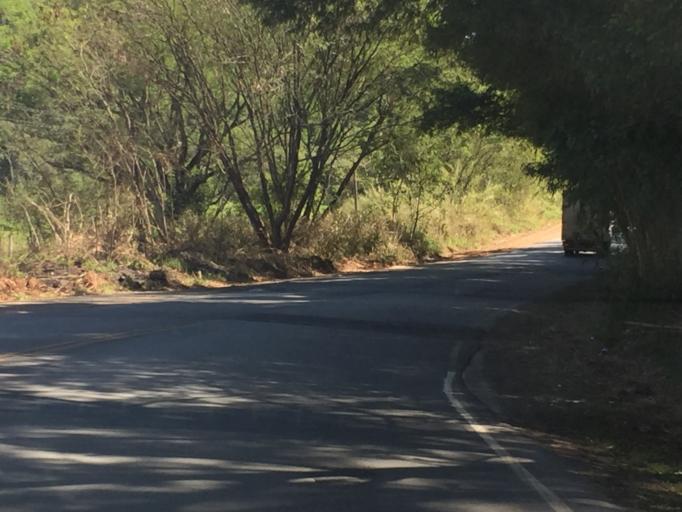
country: BR
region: Sao Paulo
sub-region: Itapira
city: Itapira
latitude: -22.4066
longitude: -46.8433
